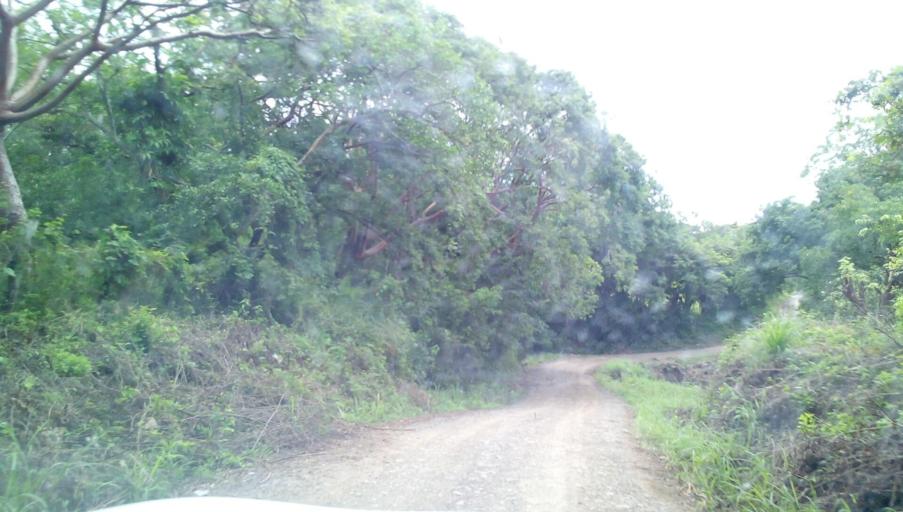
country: MX
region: Veracruz
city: Tepetzintla
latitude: 21.1359
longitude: -97.8508
